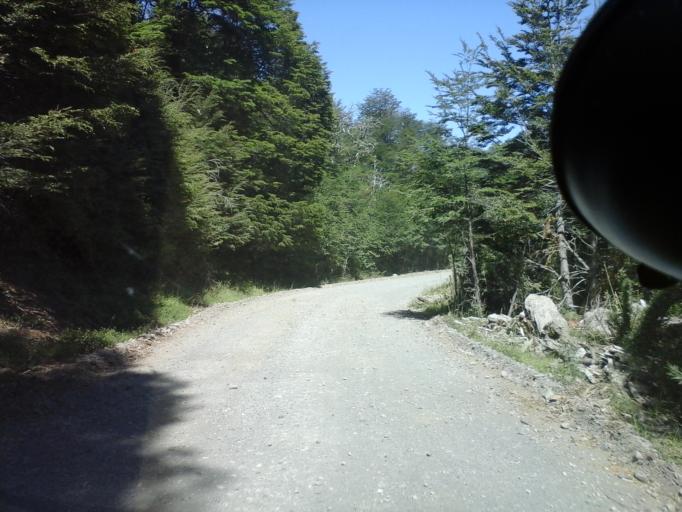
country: AR
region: Neuquen
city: Villa La Angostura
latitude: -41.2129
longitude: -71.8044
